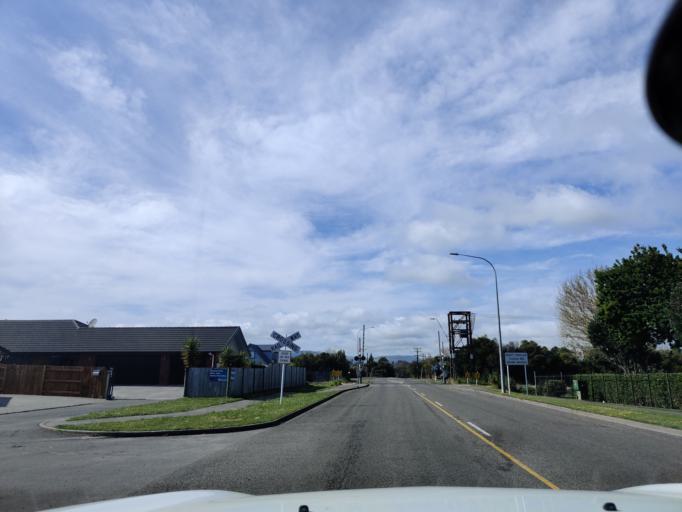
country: NZ
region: Manawatu-Wanganui
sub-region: Palmerston North City
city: Palmerston North
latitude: -40.3332
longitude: 175.6543
